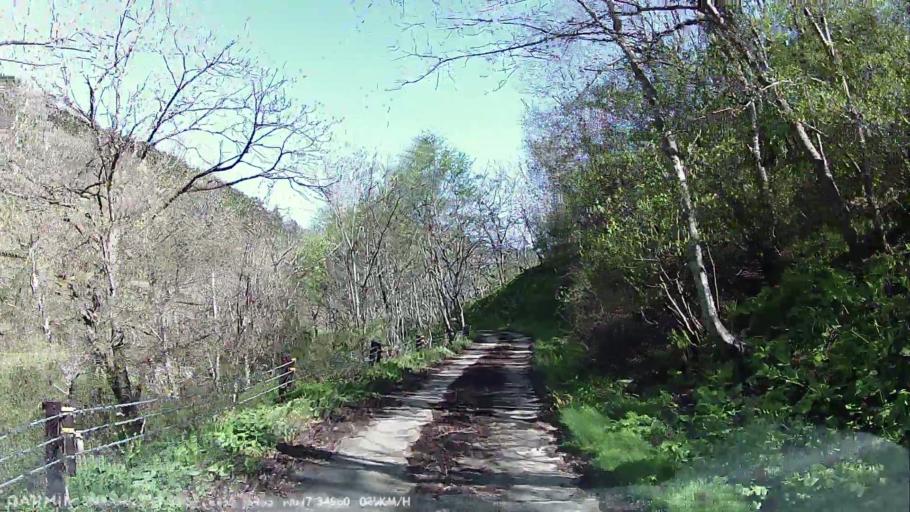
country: JP
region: Fukushima
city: Kitakata
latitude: 37.3496
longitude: 139.7846
